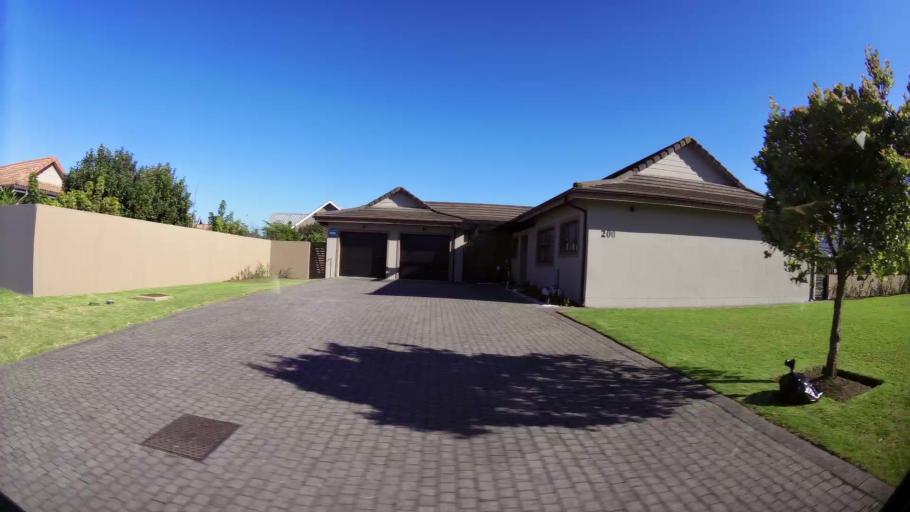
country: ZA
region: Western Cape
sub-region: Eden District Municipality
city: George
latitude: -33.9633
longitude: 22.4283
